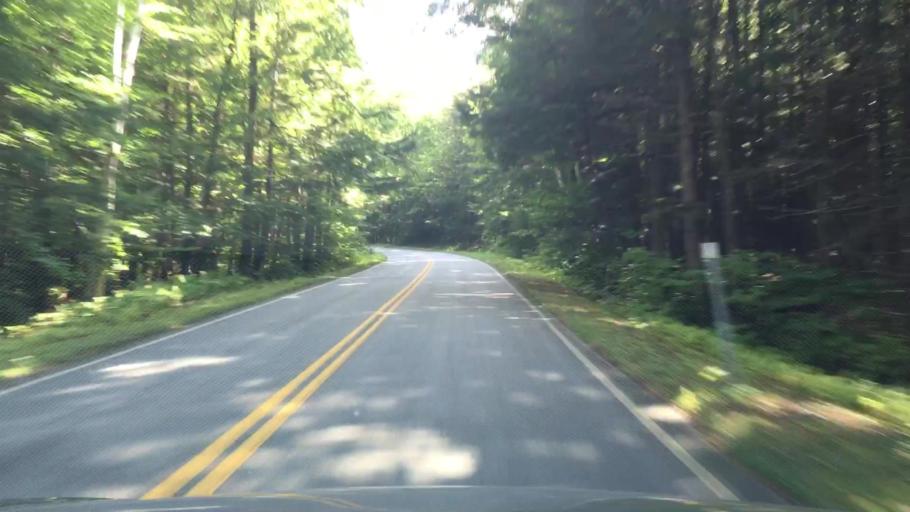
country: US
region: New Hampshire
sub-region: Carroll County
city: North Conway
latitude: 44.0650
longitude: -71.2824
